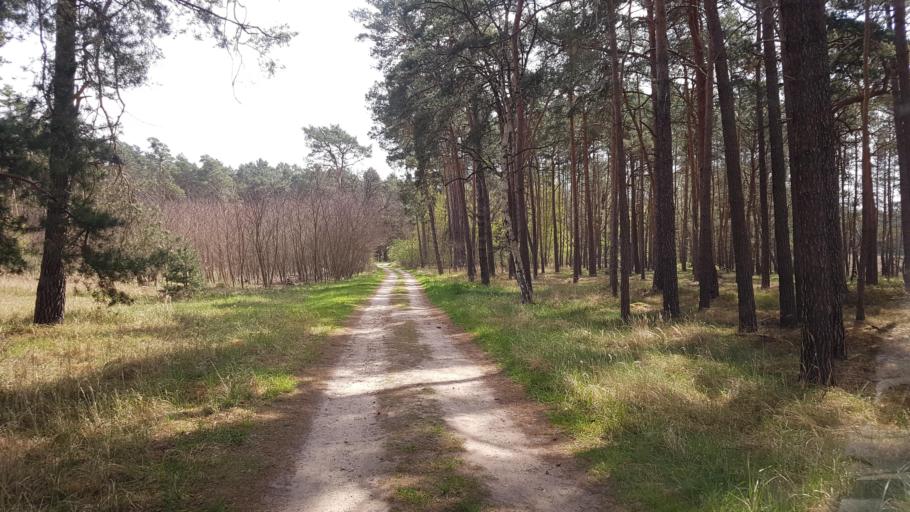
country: DE
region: Brandenburg
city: Luckenwalde
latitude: 52.1351
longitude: 13.1619
